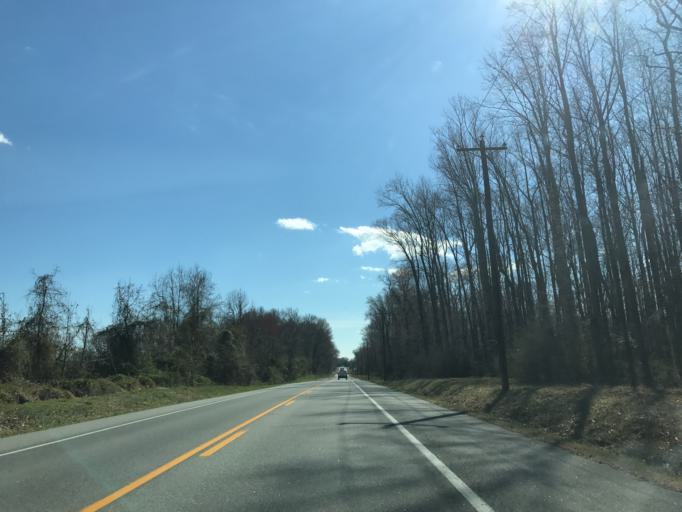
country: US
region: Maryland
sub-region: Kent County
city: Rock Hall
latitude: 39.1872
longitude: -76.1934
